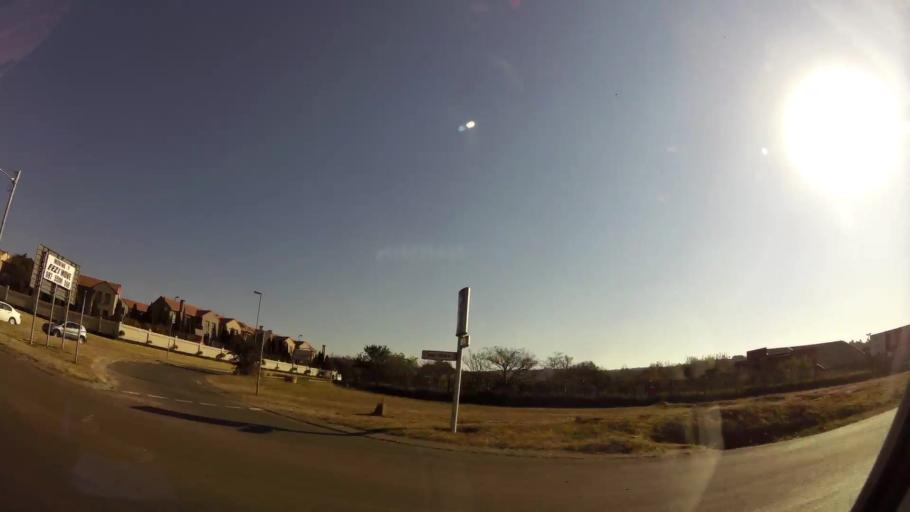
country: ZA
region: Gauteng
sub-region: City of Tshwane Metropolitan Municipality
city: Centurion
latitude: -25.8129
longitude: 28.3031
